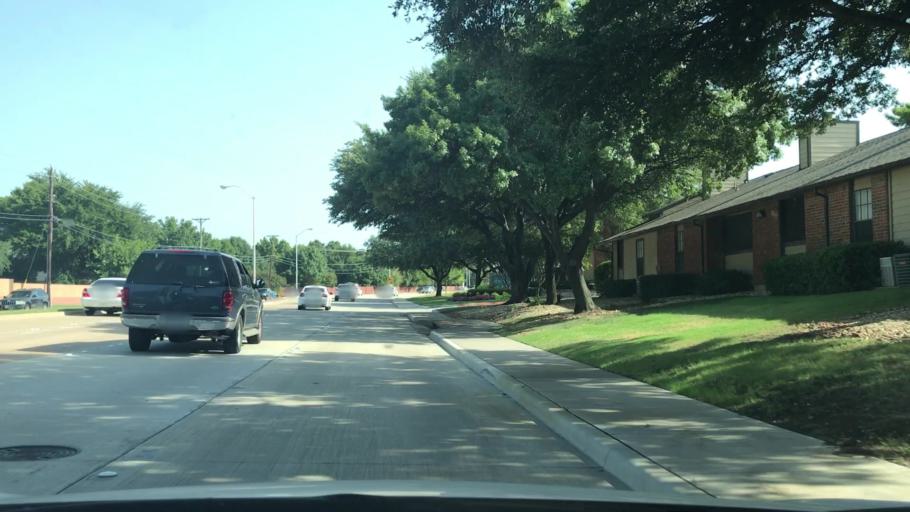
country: US
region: Texas
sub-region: Collin County
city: Plano
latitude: 33.0547
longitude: -96.7506
